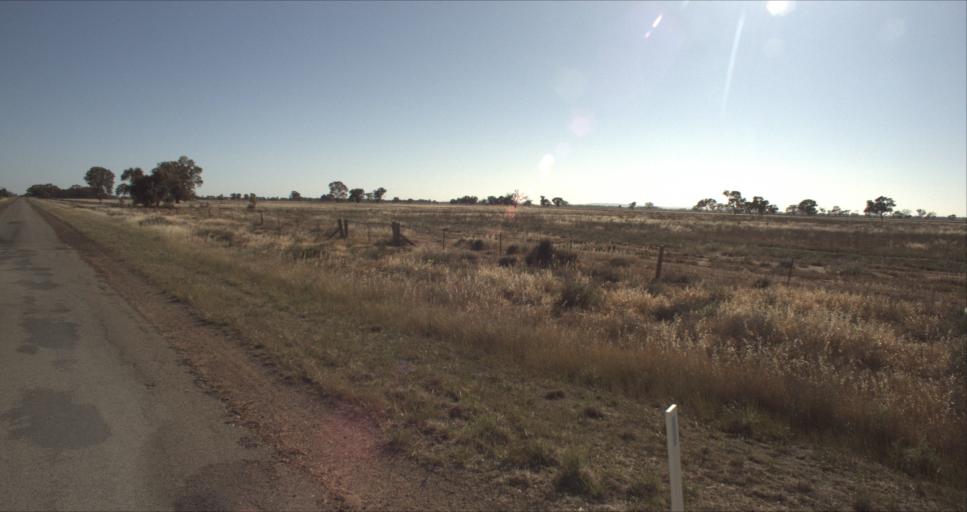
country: AU
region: New South Wales
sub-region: Leeton
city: Leeton
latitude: -34.5979
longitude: 146.2583
